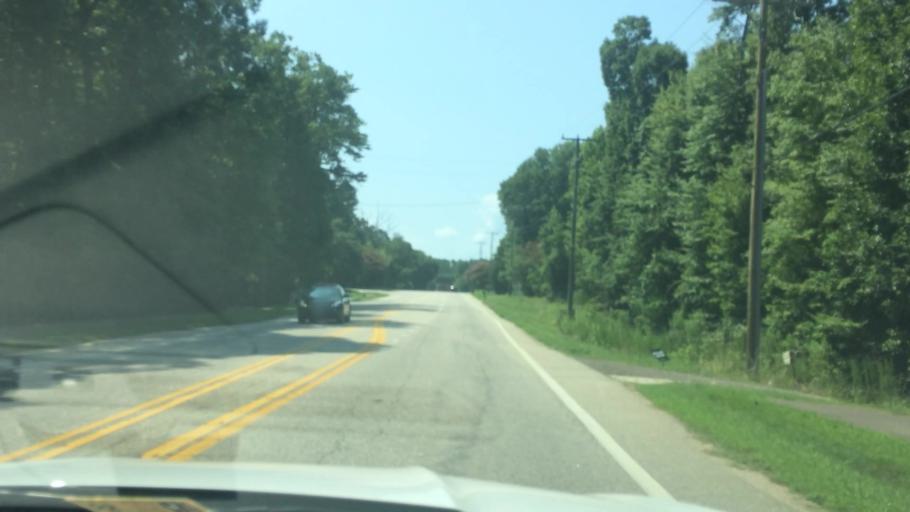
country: US
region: Virginia
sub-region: James City County
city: Williamsburg
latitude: 37.3283
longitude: -76.7888
